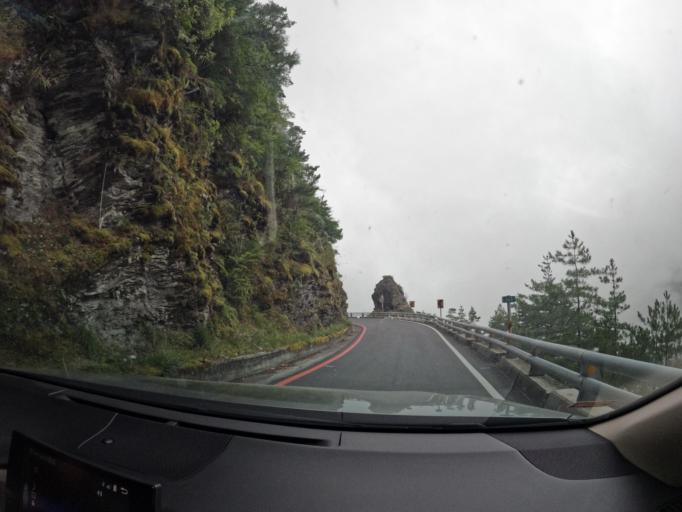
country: TW
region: Taiwan
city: Lugu
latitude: 23.2650
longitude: 120.9774
